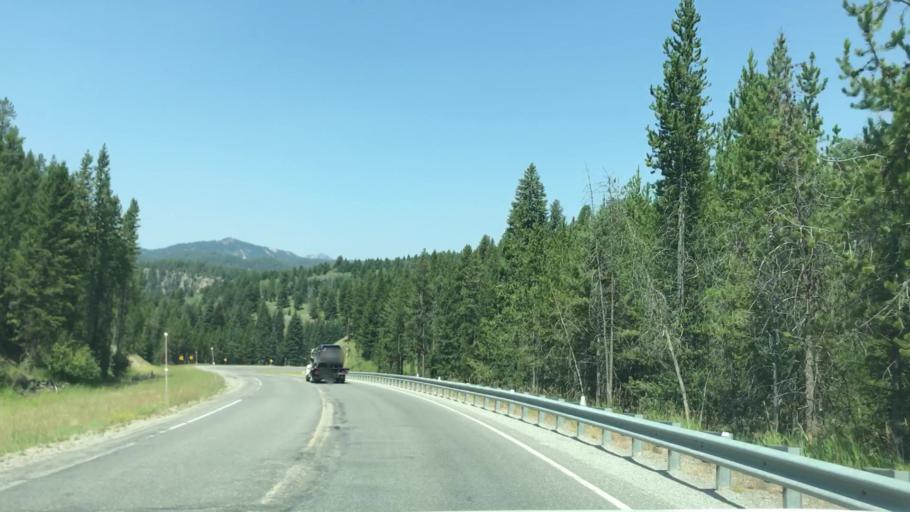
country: US
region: Montana
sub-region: Gallatin County
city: West Yellowstone
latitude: 44.7996
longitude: -111.1049
